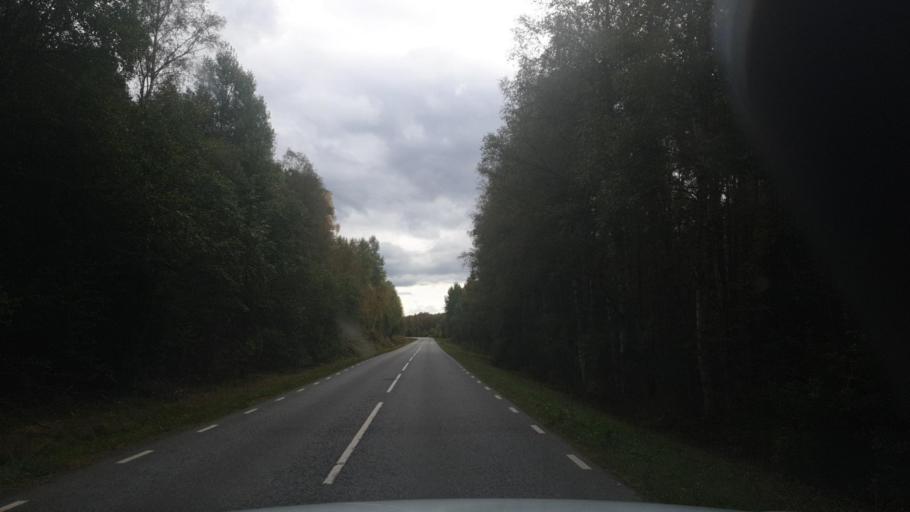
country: NO
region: Ostfold
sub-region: Romskog
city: Romskog
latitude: 59.6952
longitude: 12.0907
